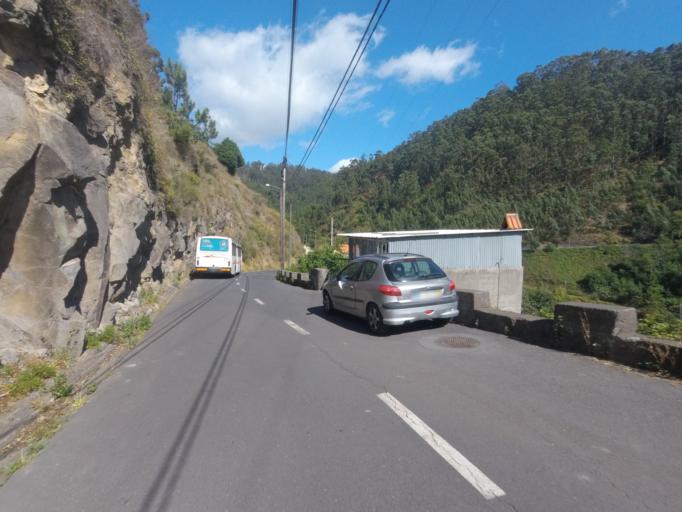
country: PT
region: Madeira
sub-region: Ribeira Brava
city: Campanario
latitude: 32.6892
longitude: -17.0307
